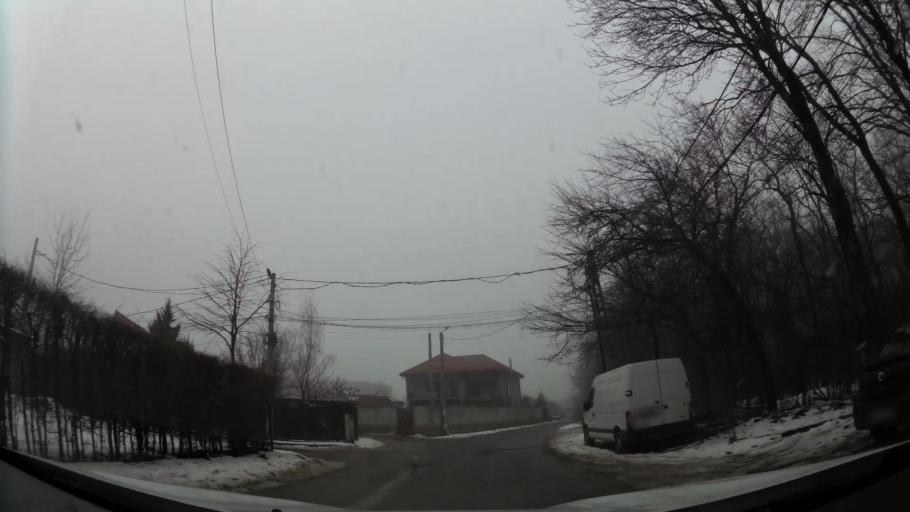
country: RO
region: Ilfov
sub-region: Comuna Chiajna
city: Rosu
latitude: 44.4539
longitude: 25.9955
